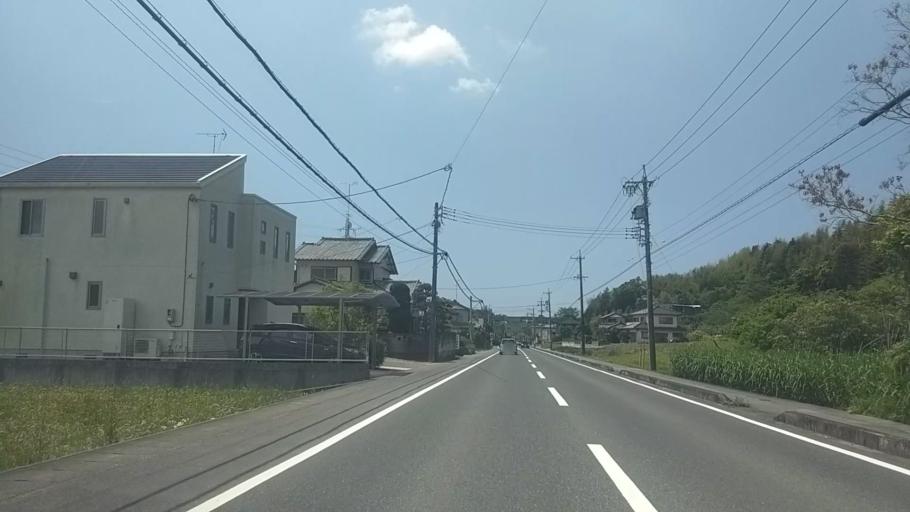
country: JP
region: Shizuoka
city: Hamamatsu
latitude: 34.7688
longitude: 137.6644
